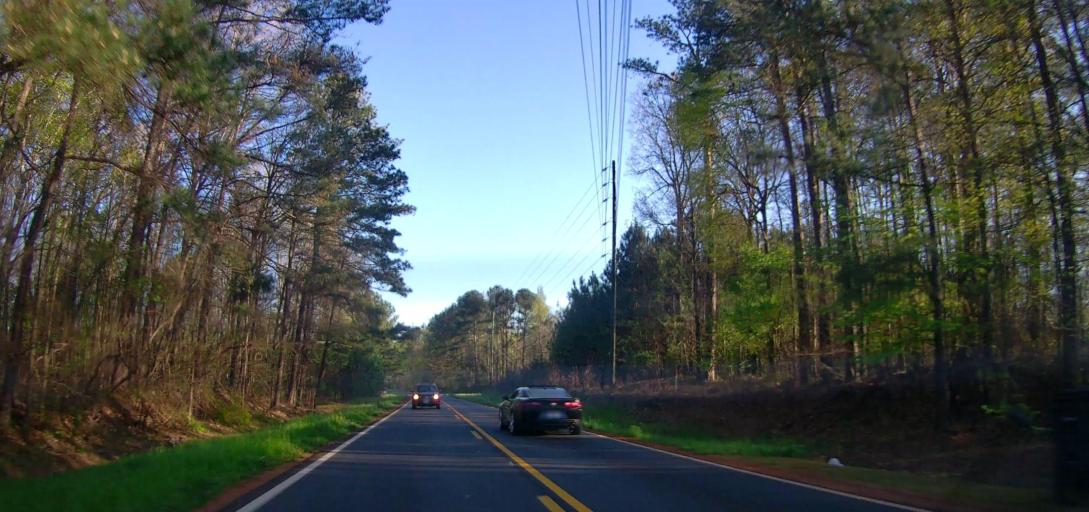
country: US
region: Georgia
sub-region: Newton County
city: Porterdale
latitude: 33.5799
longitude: -83.9068
